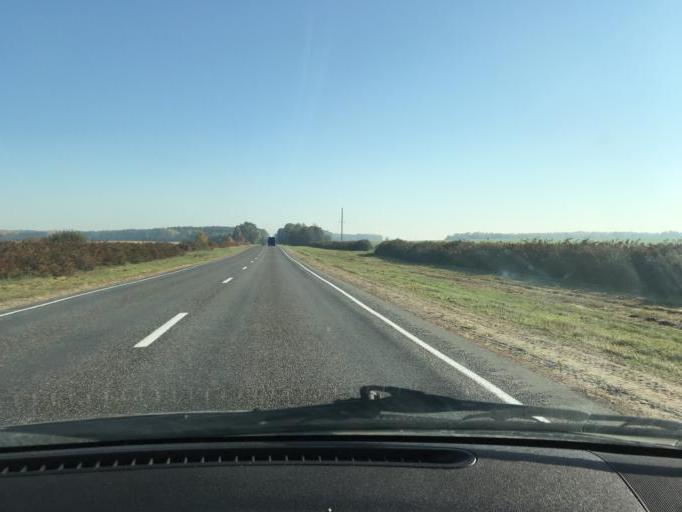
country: BY
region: Brest
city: Baranovichi
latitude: 52.9338
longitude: 26.0496
